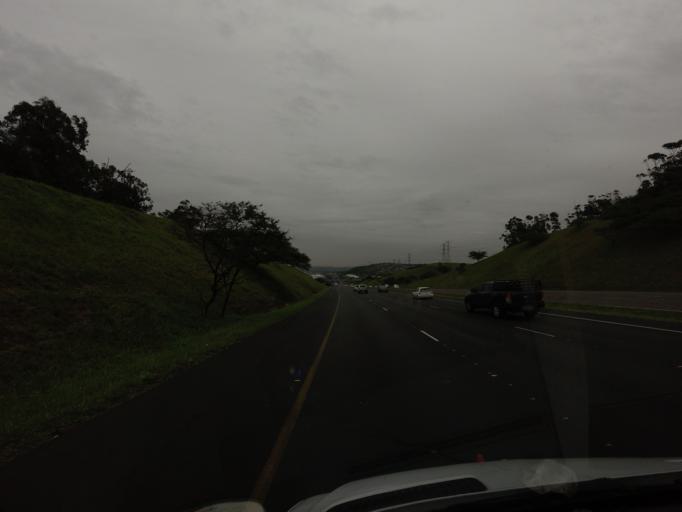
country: ZA
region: KwaZulu-Natal
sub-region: eThekwini Metropolitan Municipality
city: Berea
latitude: -29.7512
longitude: 31.0252
